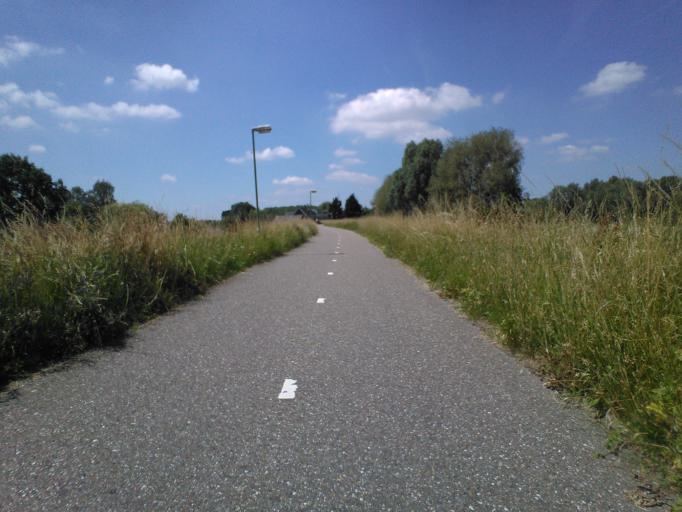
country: NL
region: South Holland
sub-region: Gemeente Gorinchem
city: Gorinchem
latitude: 51.8209
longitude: 4.9483
